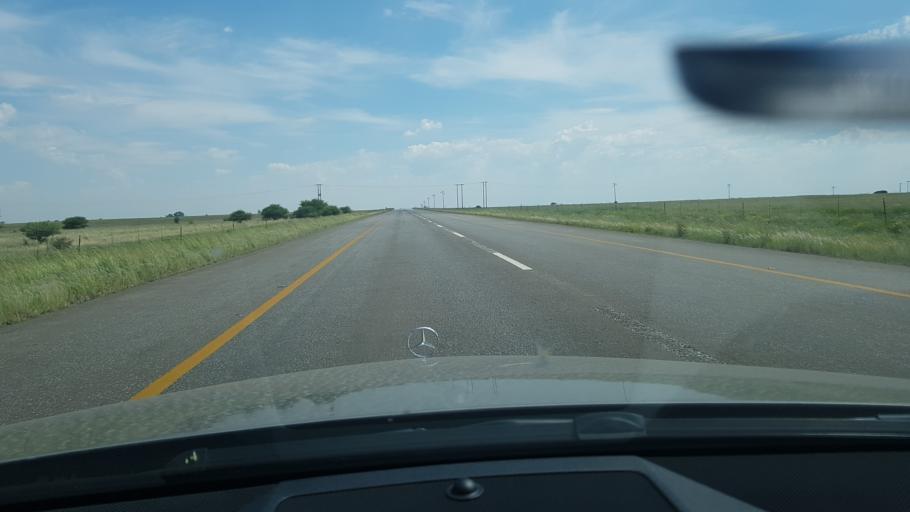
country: ZA
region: North-West
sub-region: Dr Kenneth Kaunda District Municipality
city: Wolmaransstad
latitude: -27.2899
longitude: 25.9171
